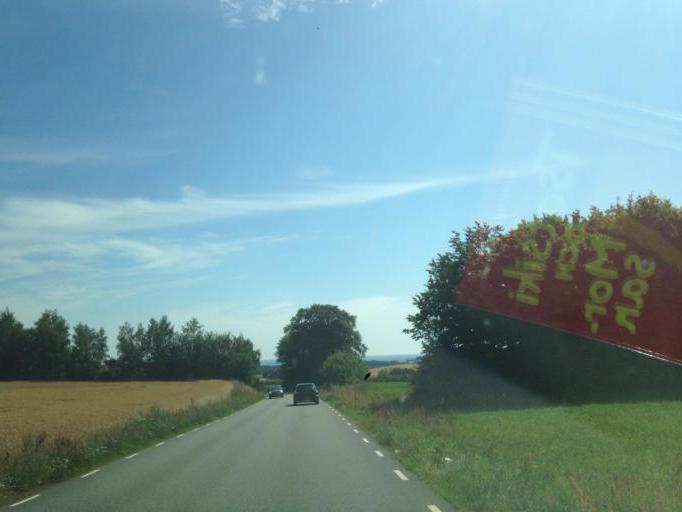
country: SE
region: Skane
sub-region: Simrishamns Kommun
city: Kivik
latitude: 55.6371
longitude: 14.2187
